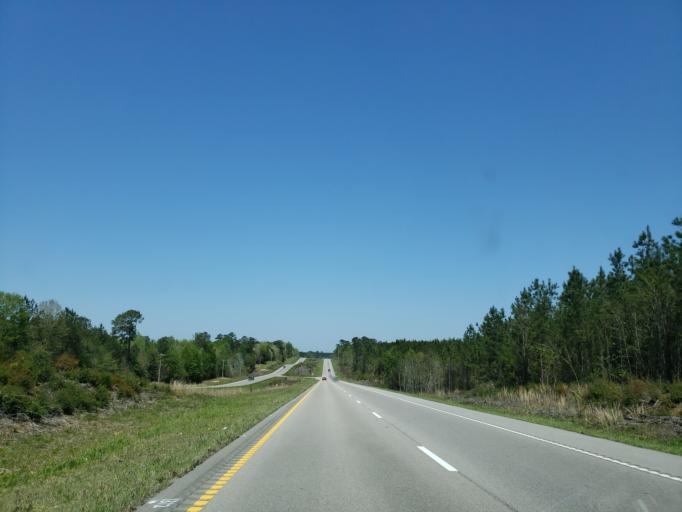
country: US
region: Mississippi
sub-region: Stone County
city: Wiggins
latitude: 30.9678
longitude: -89.1947
